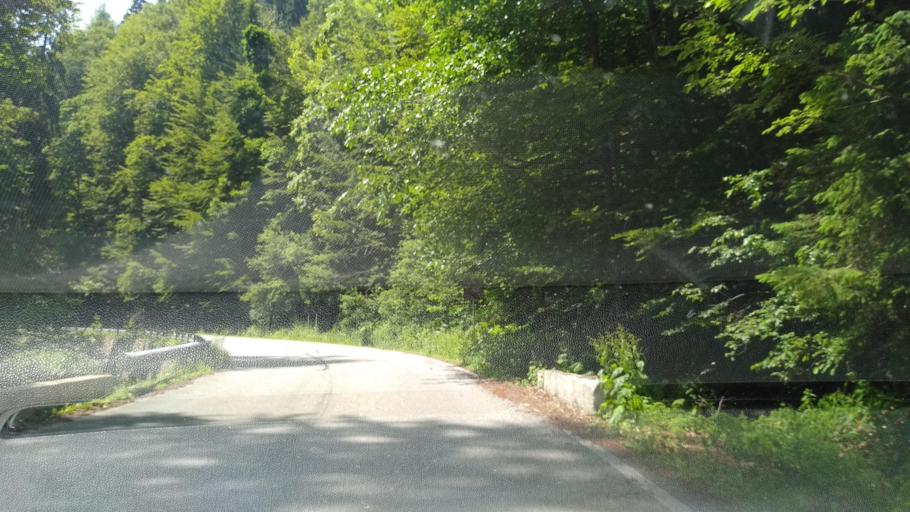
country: RO
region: Gorj
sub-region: Comuna Runcu
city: Valea Mare
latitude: 45.2736
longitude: 22.9540
